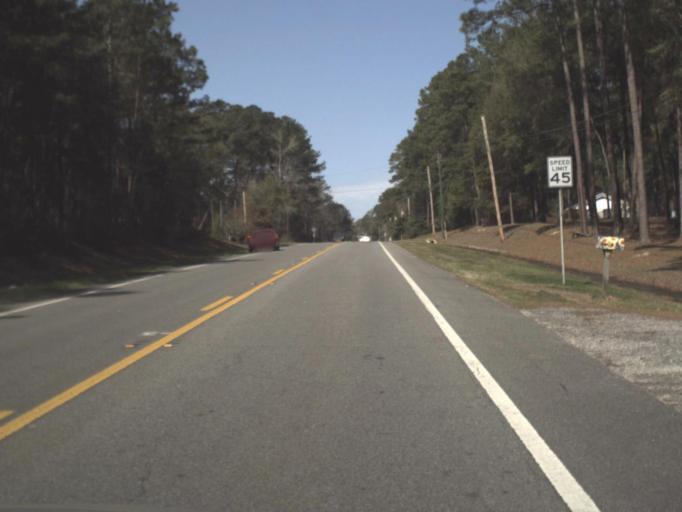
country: US
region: Florida
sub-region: Gadsden County
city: Quincy
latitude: 30.5954
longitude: -84.5326
